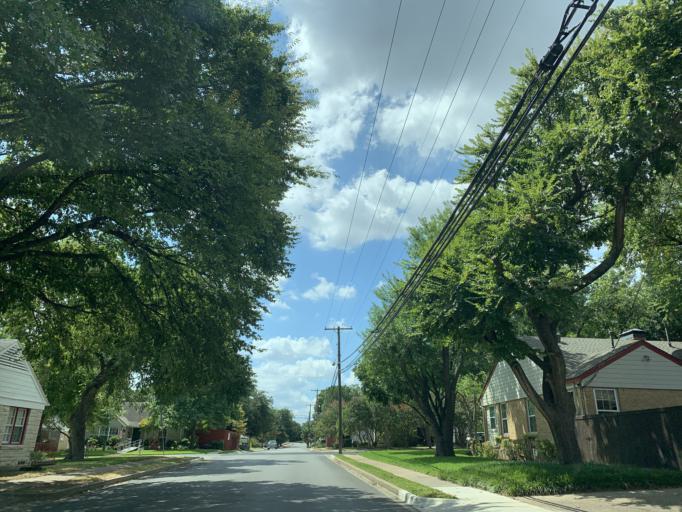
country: US
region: Texas
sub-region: Dallas County
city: Cockrell Hill
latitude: 32.7456
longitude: -96.8589
